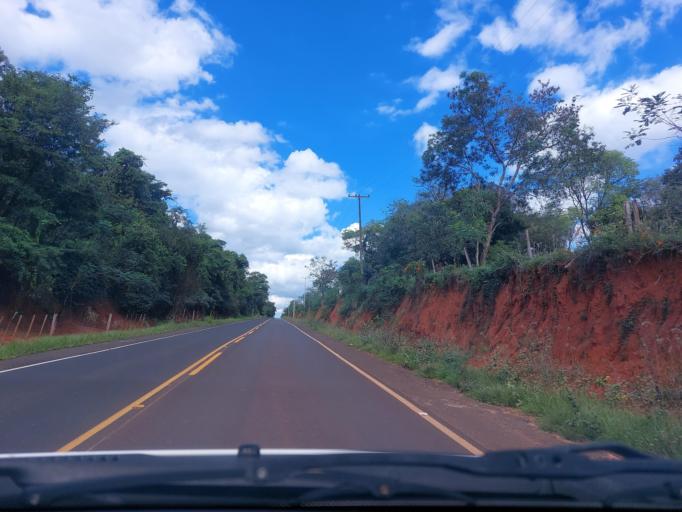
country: PY
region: San Pedro
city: Guayaybi
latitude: -24.5515
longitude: -56.5196
